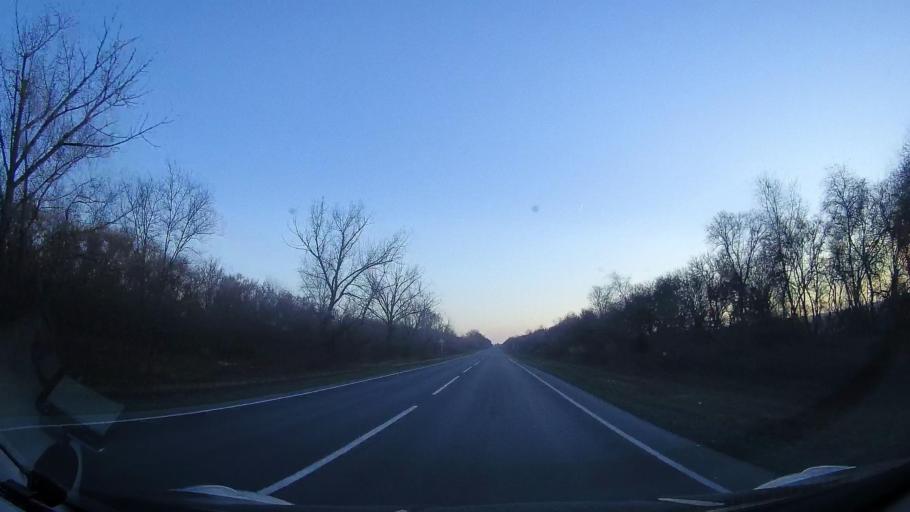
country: RU
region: Rostov
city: Bagayevskaya
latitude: 47.1340
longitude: 40.2766
